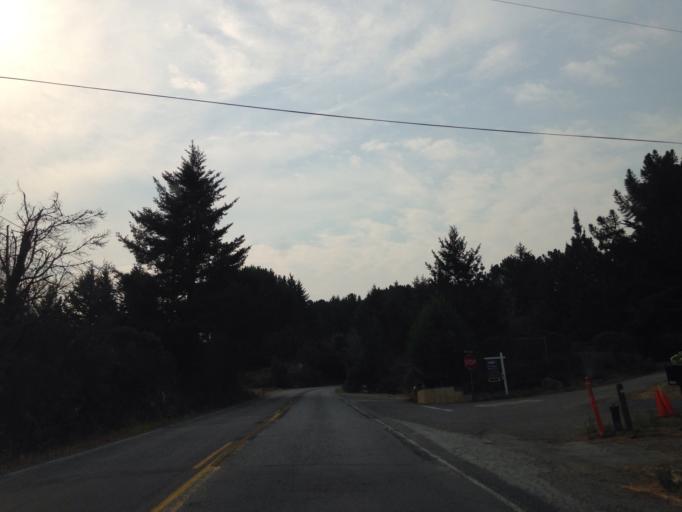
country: US
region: California
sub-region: San Mateo County
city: Highlands-Baywood Park
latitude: 37.4651
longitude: -122.3468
